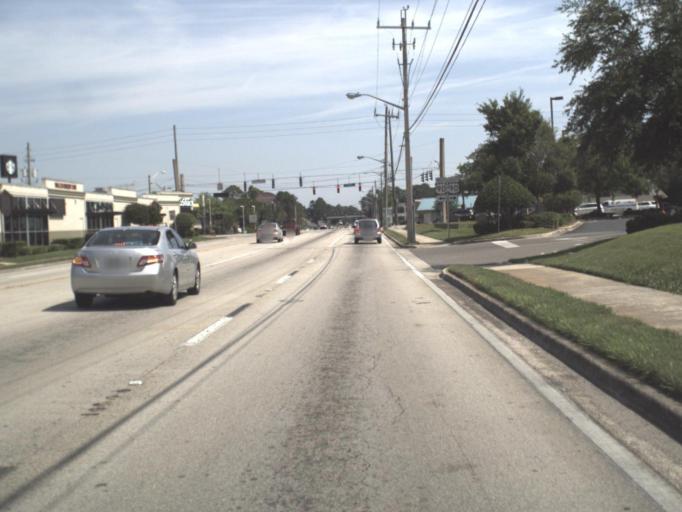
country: US
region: Florida
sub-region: Duval County
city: Jacksonville
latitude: 30.2913
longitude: -81.6020
